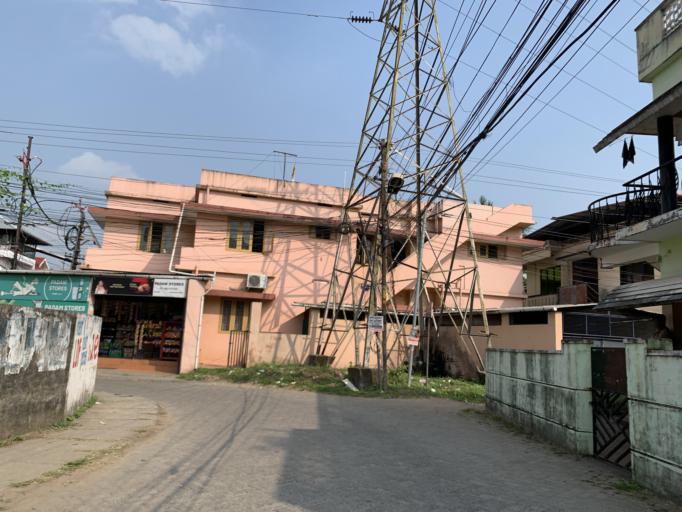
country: IN
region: Kerala
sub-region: Ernakulam
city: Cochin
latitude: 9.9569
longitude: 76.3042
